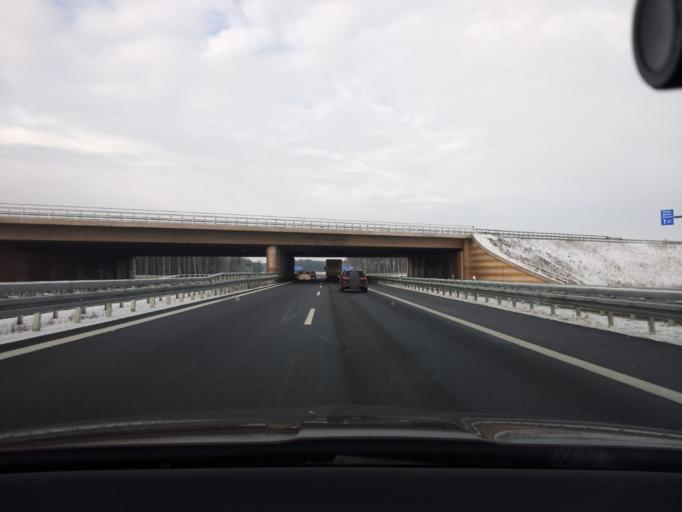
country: DE
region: Mecklenburg-Vorpommern
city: Gross Laasch
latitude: 53.4233
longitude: 11.5222
